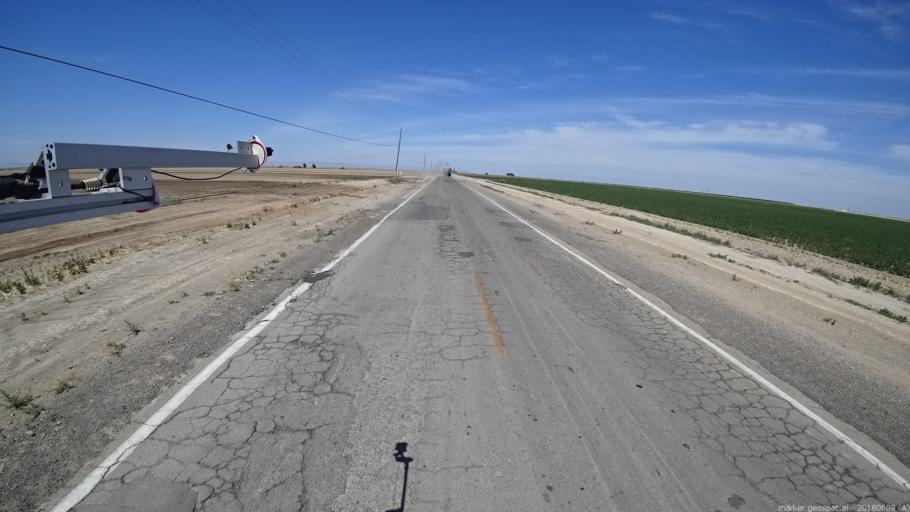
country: US
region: California
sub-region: Fresno County
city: Firebaugh
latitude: 36.9527
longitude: -120.3402
